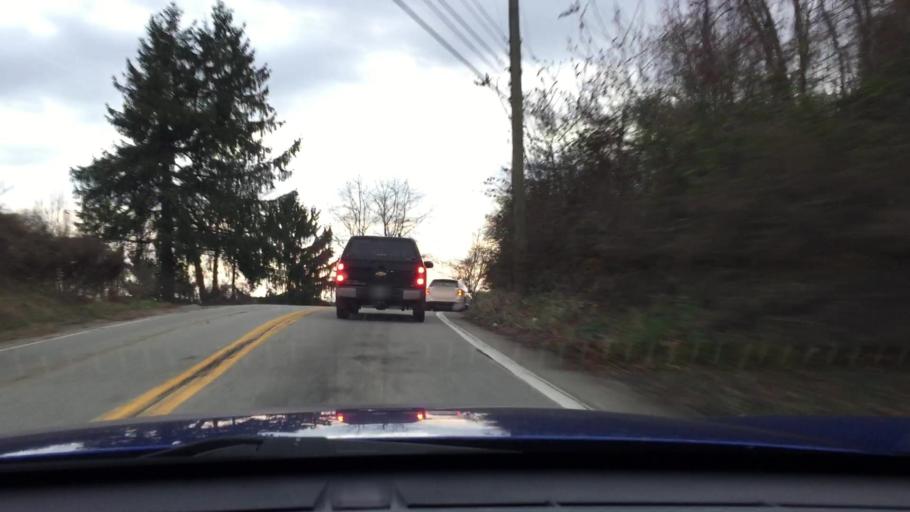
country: US
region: Pennsylvania
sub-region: Allegheny County
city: Elizabeth
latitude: 40.2360
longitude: -79.8563
